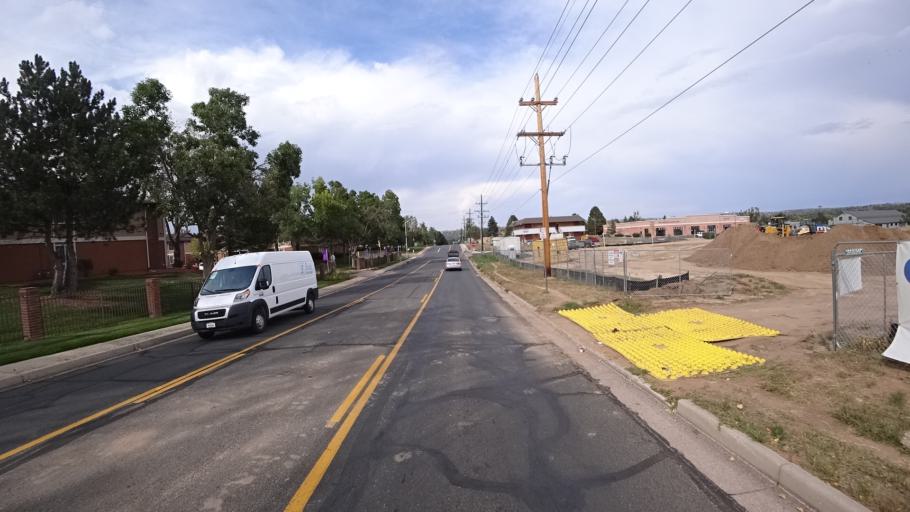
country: US
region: Colorado
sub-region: El Paso County
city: Cimarron Hills
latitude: 38.8816
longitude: -104.7609
